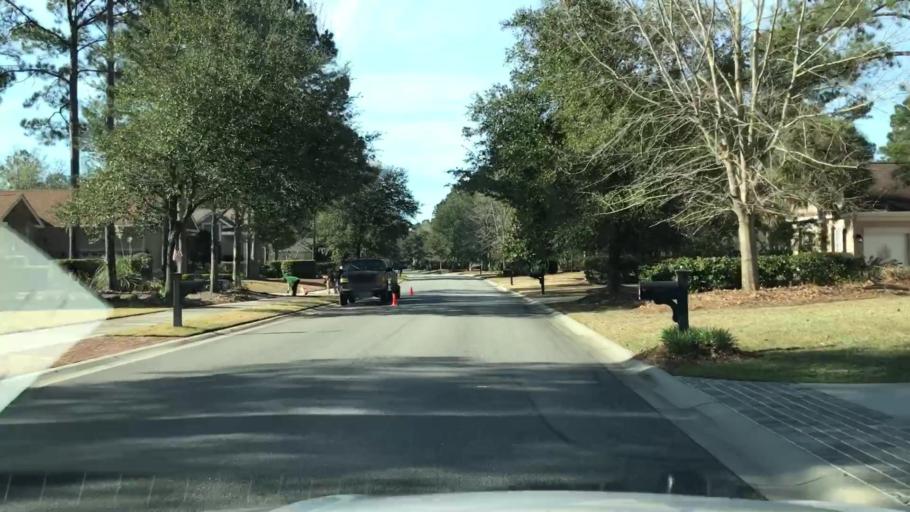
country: US
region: South Carolina
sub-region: Beaufort County
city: Bluffton
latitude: 32.2533
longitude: -80.9103
